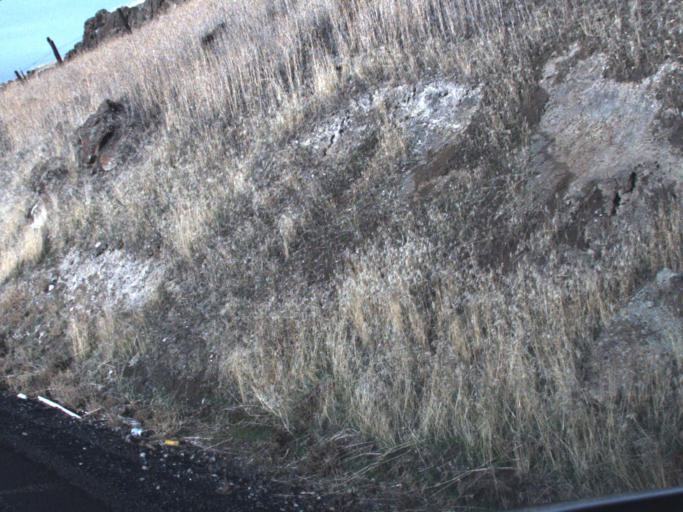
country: US
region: Washington
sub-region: Garfield County
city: Pomeroy
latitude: 46.4912
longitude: -117.7660
